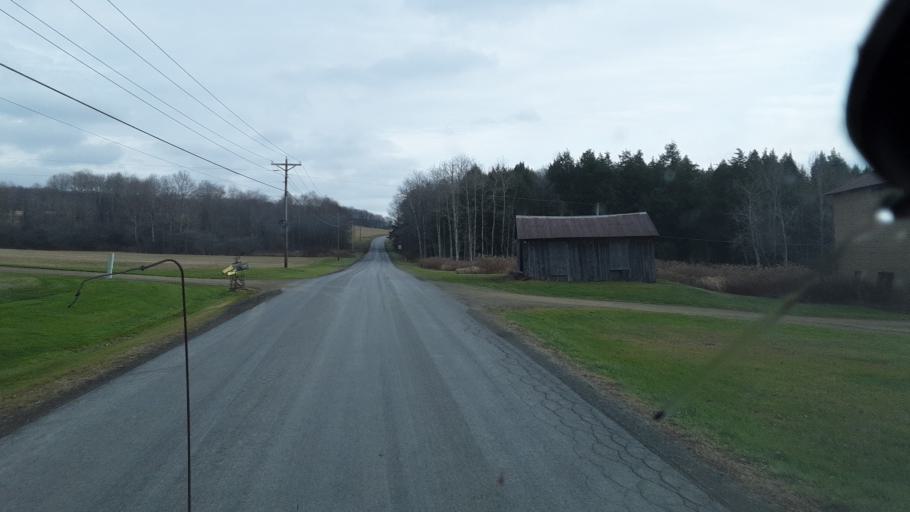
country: US
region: Pennsylvania
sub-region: Potter County
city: Galeton
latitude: 41.8877
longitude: -77.7759
